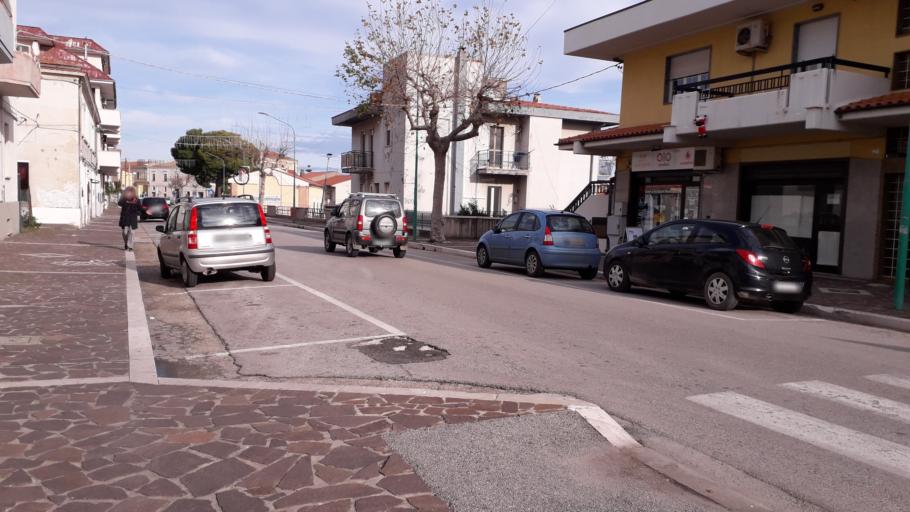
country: IT
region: Molise
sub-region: Provincia di Campobasso
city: Campomarino
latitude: 41.9551
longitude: 15.0355
